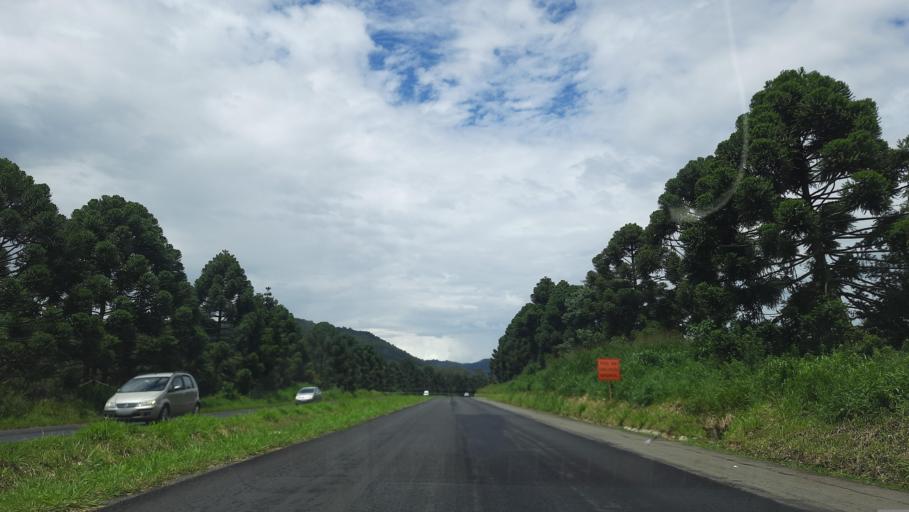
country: BR
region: Minas Gerais
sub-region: Pocos De Caldas
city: Pocos de Caldas
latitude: -21.8143
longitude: -46.6600
